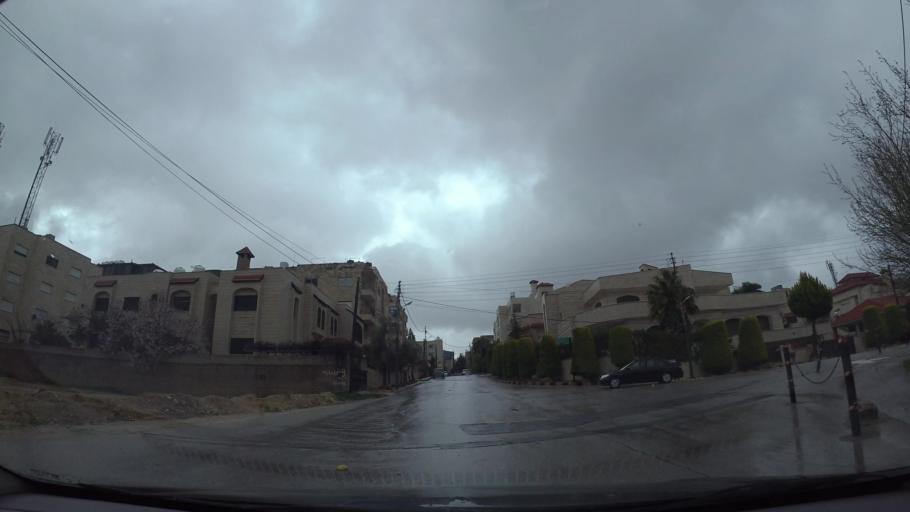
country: JO
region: Amman
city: Al Jubayhah
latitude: 32.0241
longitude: 35.8725
